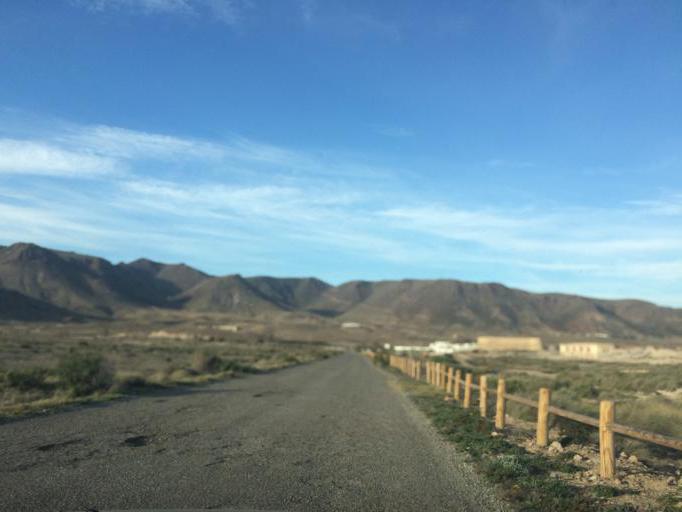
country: ES
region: Andalusia
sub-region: Provincia de Almeria
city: San Jose
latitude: 36.7986
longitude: -2.0634
